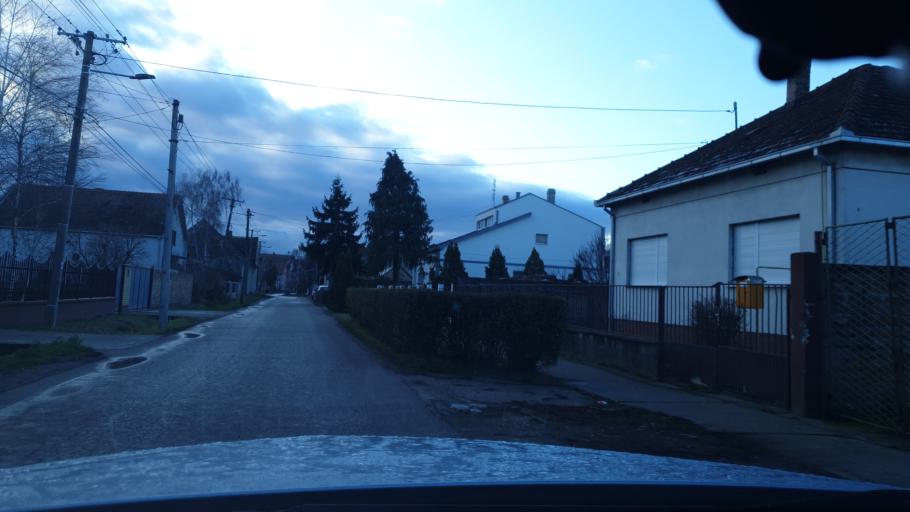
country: RS
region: Autonomna Pokrajina Vojvodina
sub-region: Sremski Okrug
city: Stara Pazova
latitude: 44.9865
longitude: 20.1657
